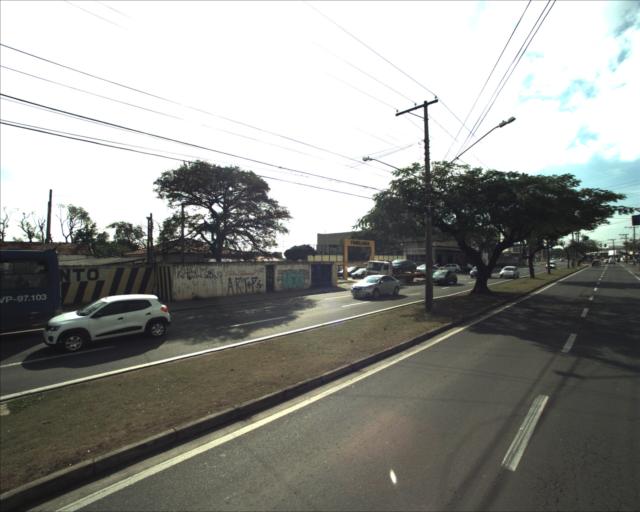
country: BR
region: Sao Paulo
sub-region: Sorocaba
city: Sorocaba
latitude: -23.5163
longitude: -47.4896
